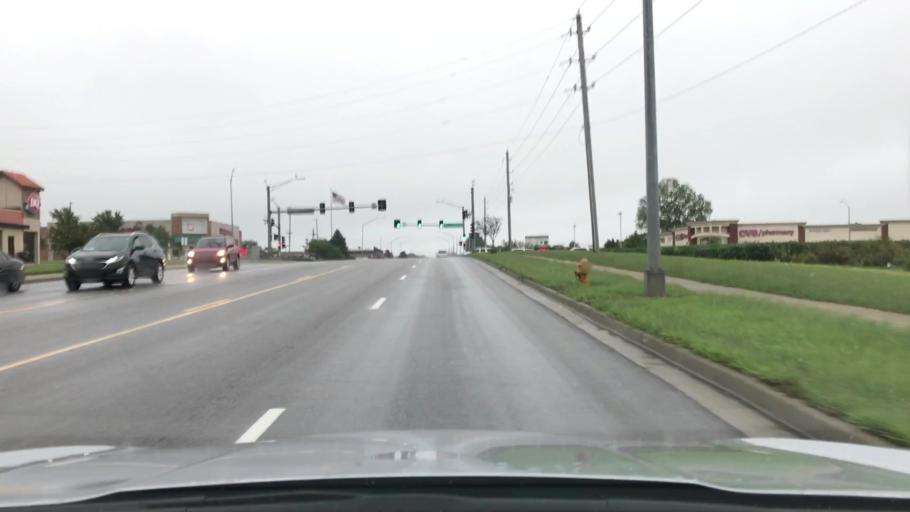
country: US
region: Missouri
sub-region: Cass County
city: Raymore
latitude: 38.8121
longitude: -94.4778
